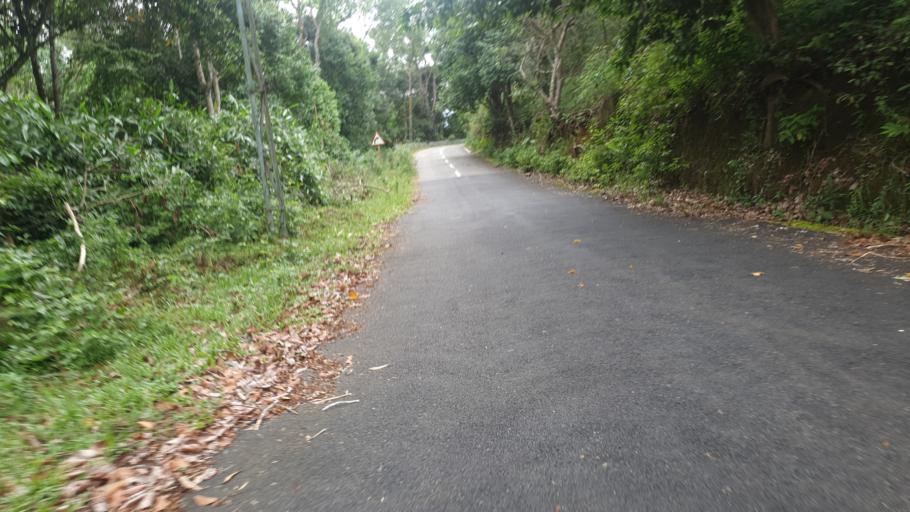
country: IN
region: Kerala
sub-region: Thiruvananthapuram
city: Nedumangad
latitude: 8.6303
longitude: 77.1274
